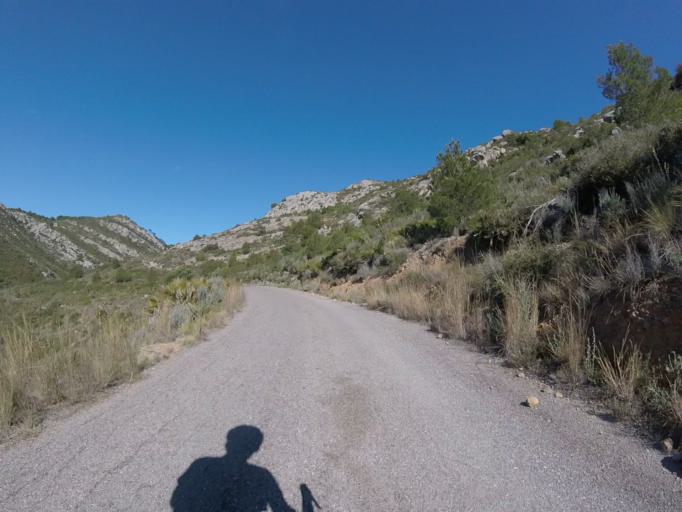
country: ES
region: Valencia
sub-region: Provincia de Castello
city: Orpesa/Oropesa del Mar
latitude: 40.0768
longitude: 0.1078
